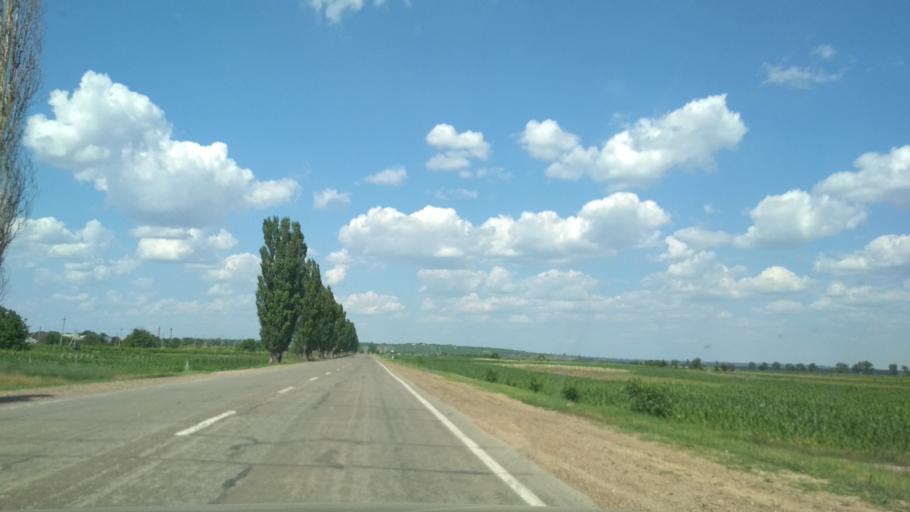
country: MD
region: Chisinau
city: Vadul lui Voda
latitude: 47.1375
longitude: 29.1344
